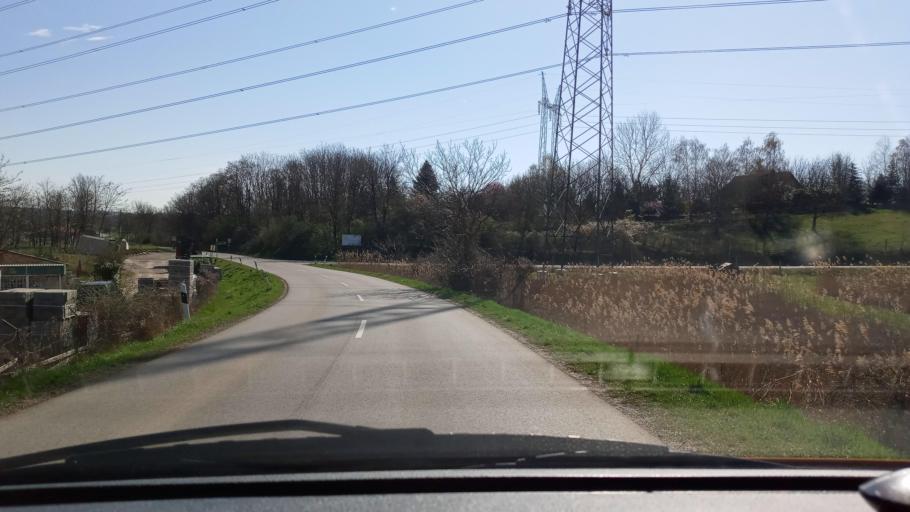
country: HU
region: Baranya
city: Kozarmisleny
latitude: 46.0843
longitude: 18.3069
